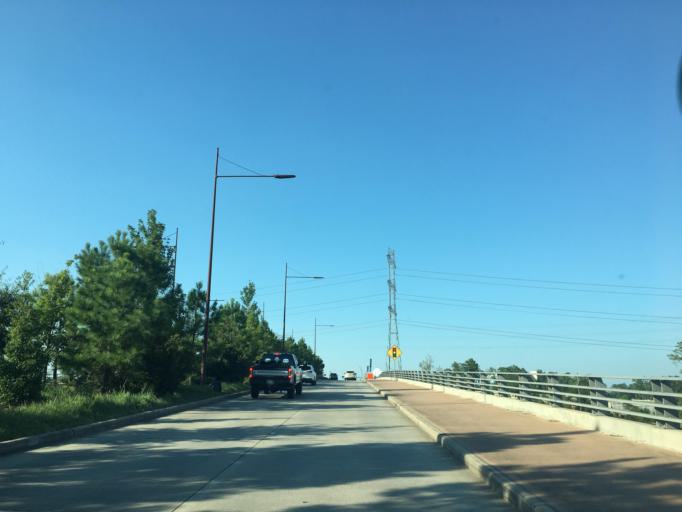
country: US
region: Texas
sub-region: Harris County
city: Spring
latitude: 30.0851
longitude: -95.4506
